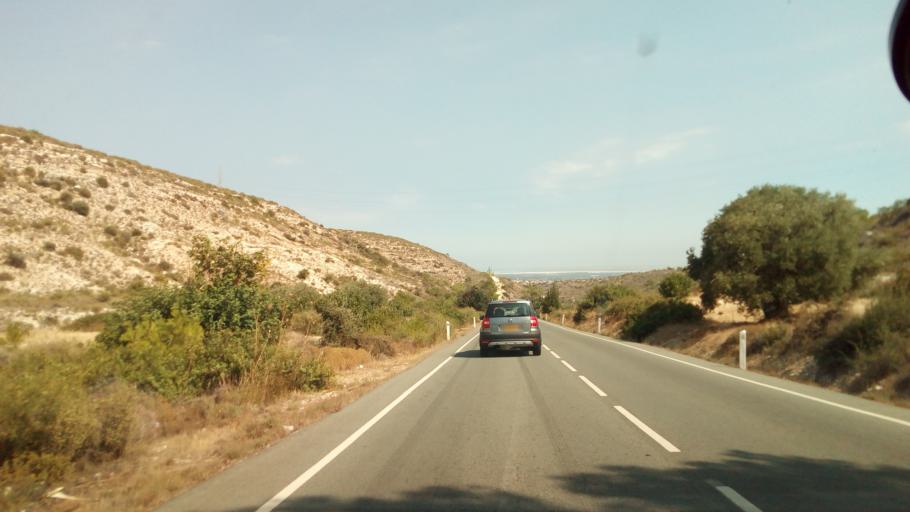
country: CY
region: Limassol
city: Sotira
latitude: 34.7030
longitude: 32.8949
